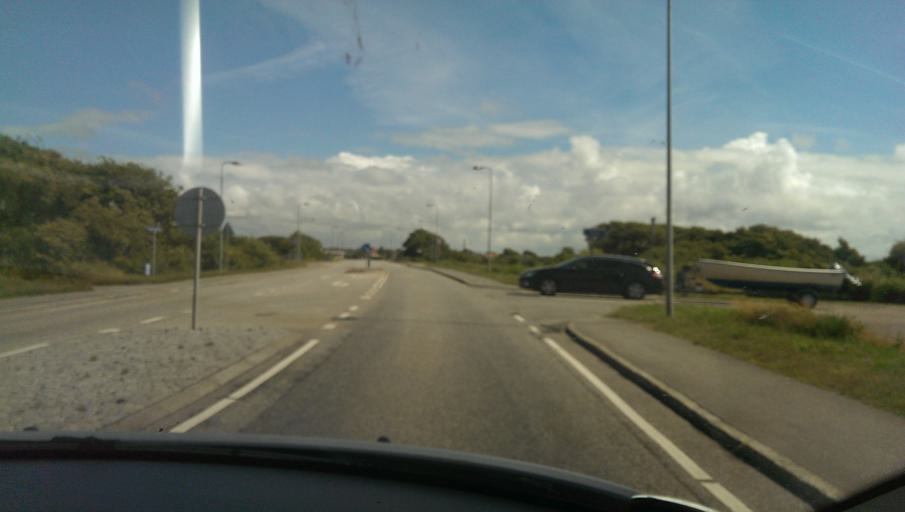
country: DK
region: Central Jutland
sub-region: Ringkobing-Skjern Kommune
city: Ringkobing
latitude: 56.0967
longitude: 8.2301
